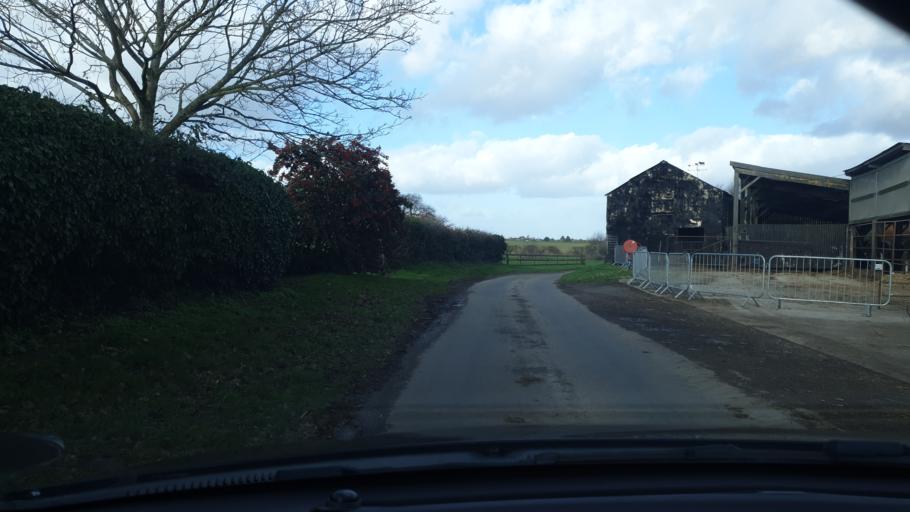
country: GB
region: England
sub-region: Essex
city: Manningtree
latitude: 51.9303
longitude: 1.0604
